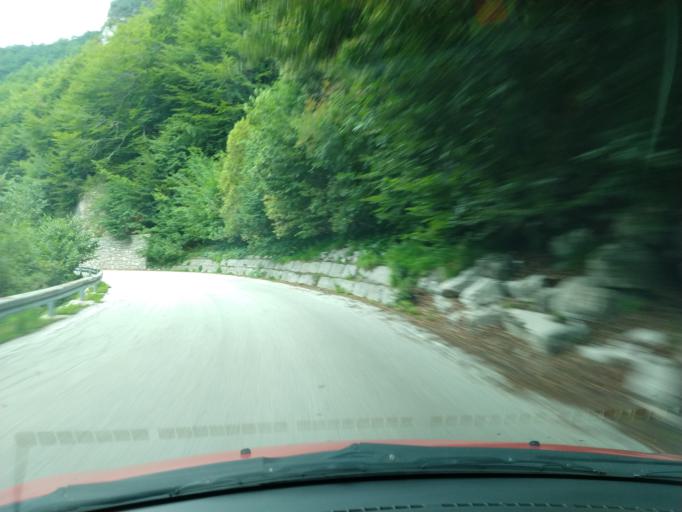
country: IT
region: Veneto
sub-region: Provincia di Vicenza
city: Tonezza del Cimone
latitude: 45.8736
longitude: 11.3274
